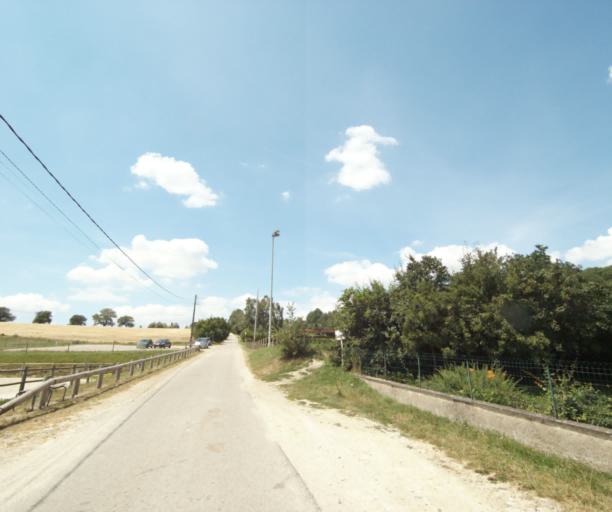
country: FR
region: Lorraine
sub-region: Departement de Meurthe-et-Moselle
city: Luneville
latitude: 48.6025
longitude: 6.4609
